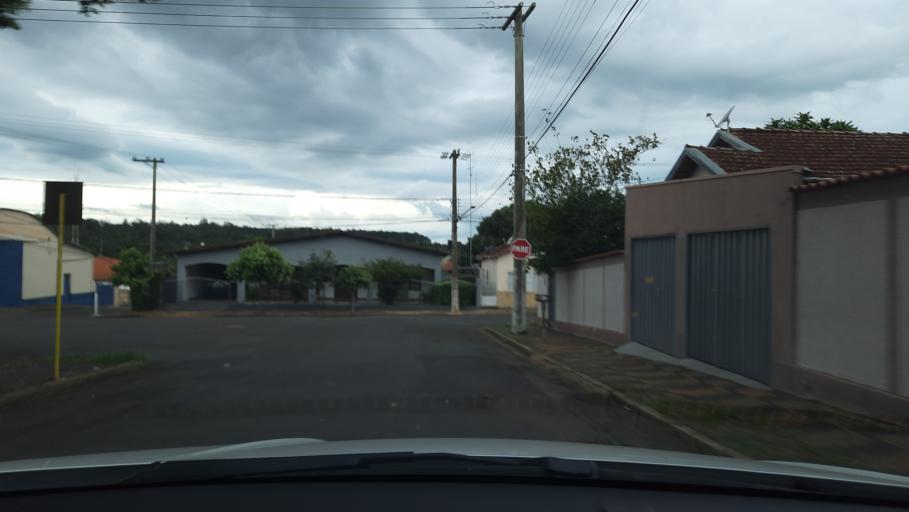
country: BR
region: Sao Paulo
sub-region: Casa Branca
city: Casa Branca
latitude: -21.7775
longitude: -47.0759
